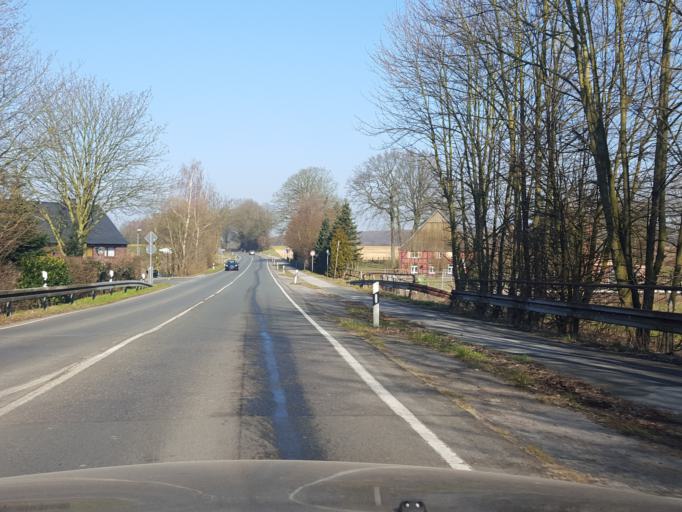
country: DE
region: North Rhine-Westphalia
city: Oer-Erkenschwick
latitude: 51.6486
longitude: 7.2324
